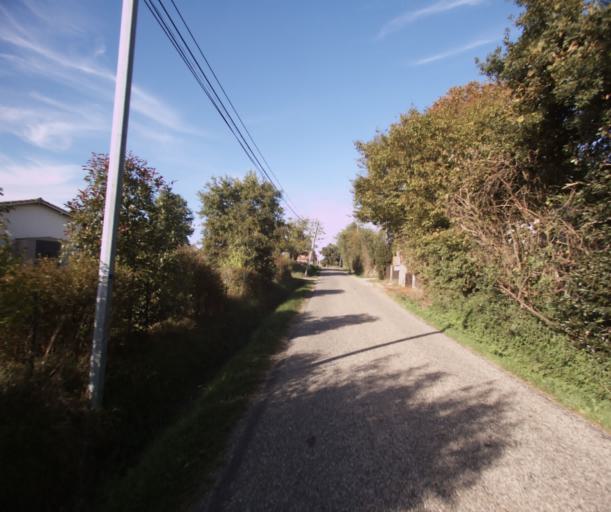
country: FR
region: Midi-Pyrenees
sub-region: Departement du Gers
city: Eauze
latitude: 43.8682
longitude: 0.0295
